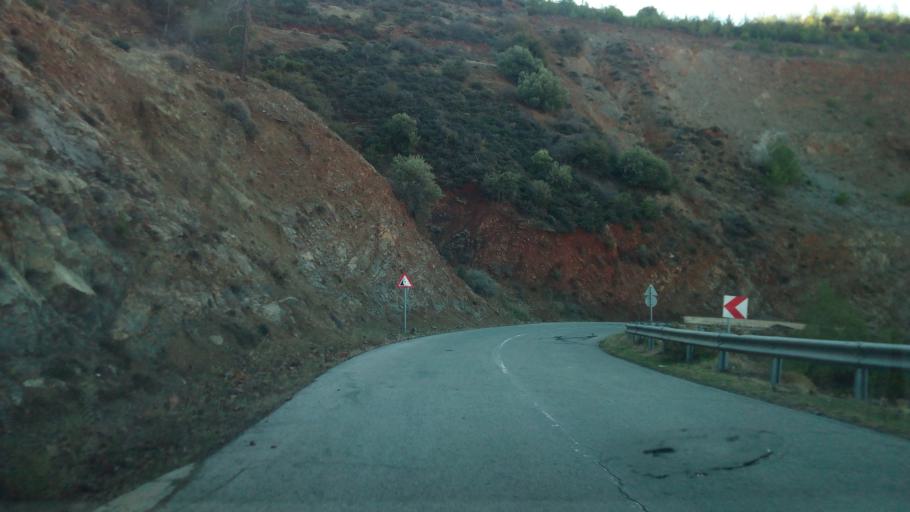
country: CY
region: Lefkosia
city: Lefka
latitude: 35.0729
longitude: 32.8175
